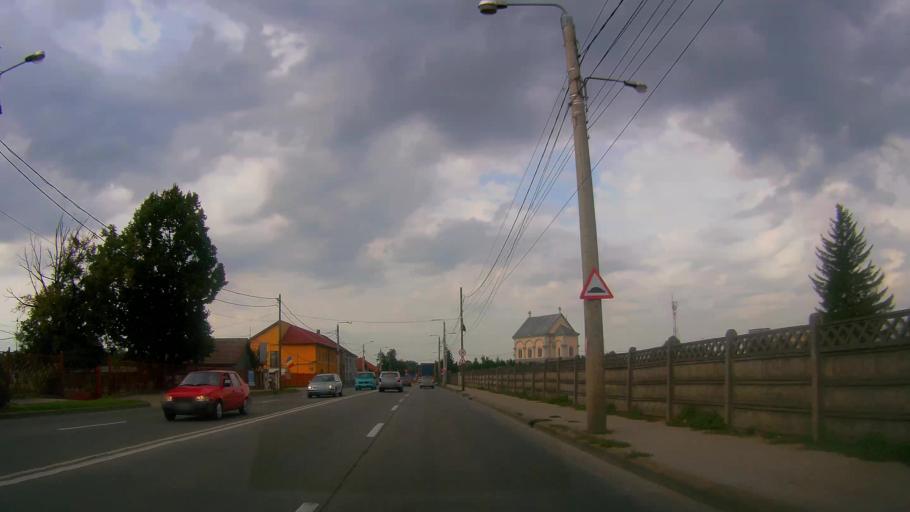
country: RO
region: Satu Mare
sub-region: Municipiul Satu Mare
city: Satu Mare
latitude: 47.7927
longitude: 22.8927
